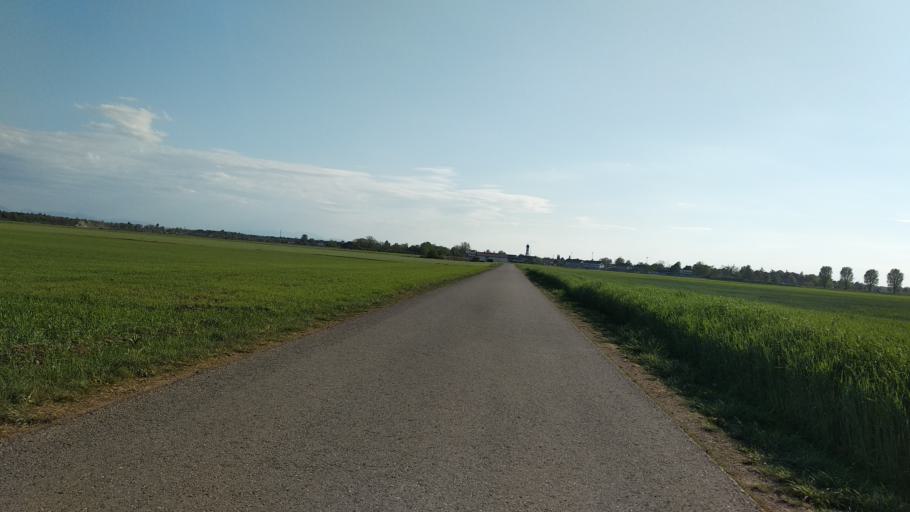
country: DE
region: Bavaria
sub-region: Upper Bavaria
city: Hohenbrunn
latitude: 48.0564
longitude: 11.7133
